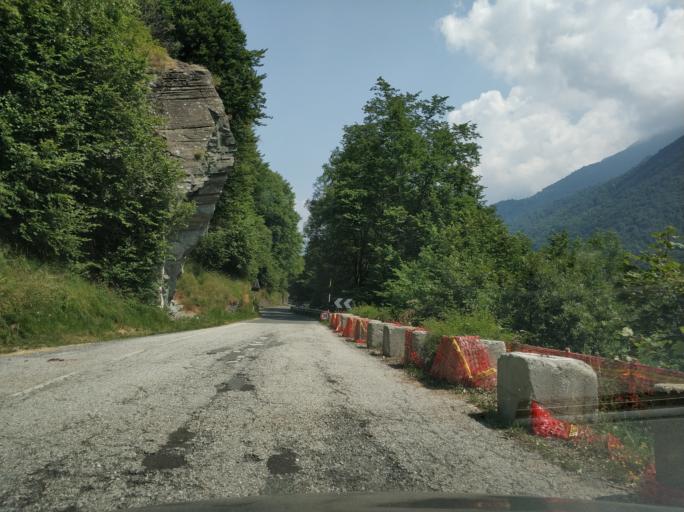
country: IT
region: Piedmont
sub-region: Provincia di Torino
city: Lemie
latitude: 45.2268
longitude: 7.2571
